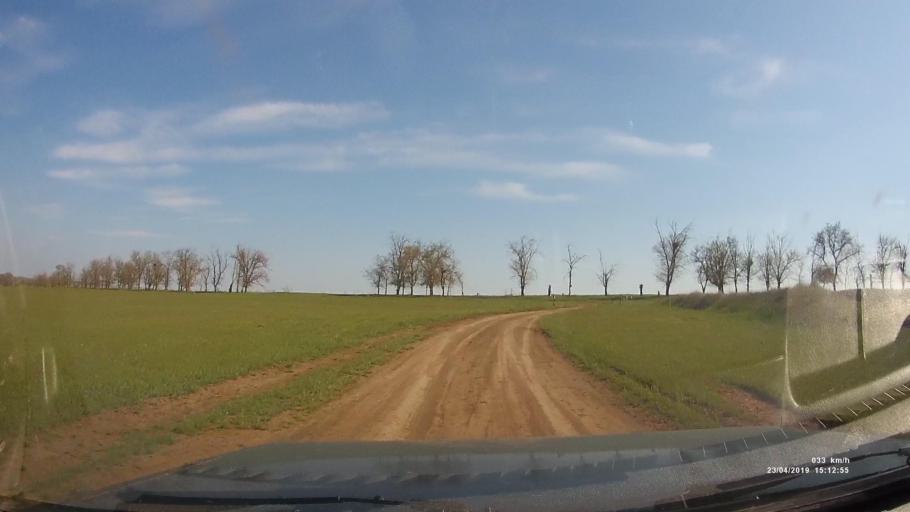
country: RU
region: Rostov
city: Remontnoye
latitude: 46.5407
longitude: 42.9527
